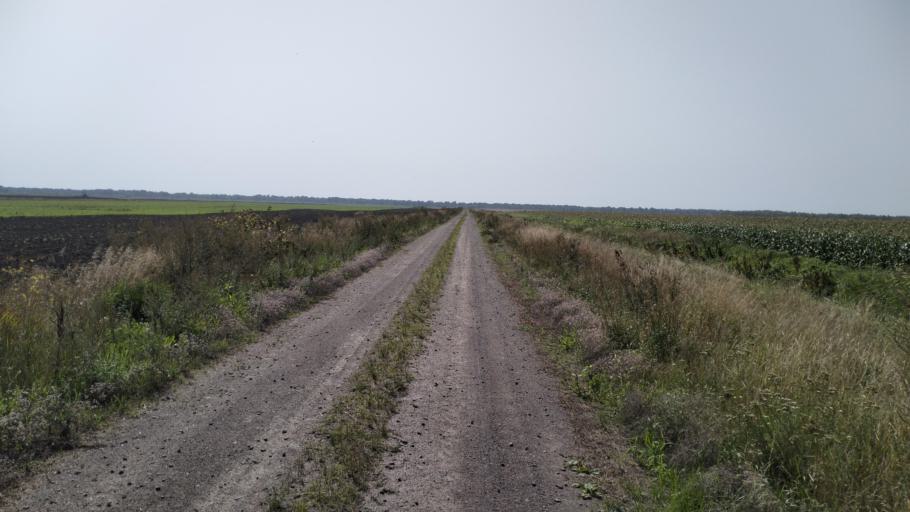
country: BY
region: Brest
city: Davyd-Haradok
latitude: 51.9870
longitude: 27.1640
